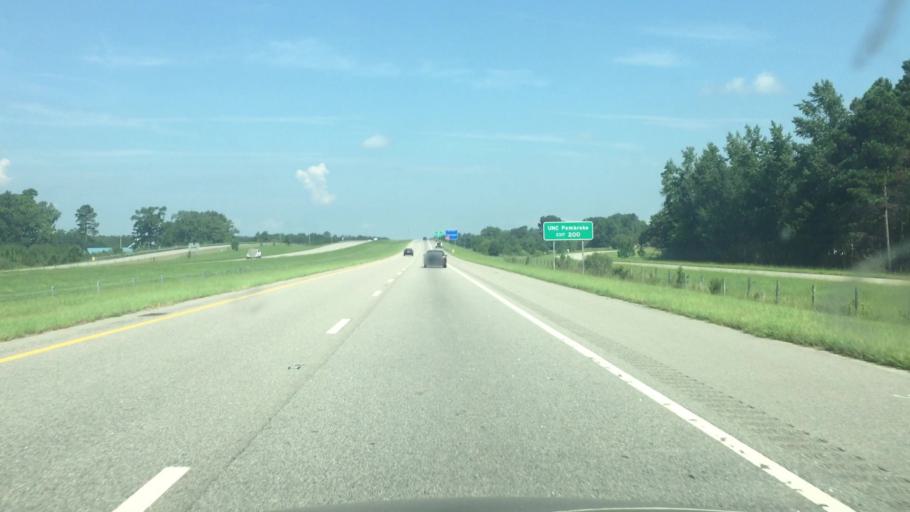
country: US
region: North Carolina
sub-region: Robeson County
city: Pembroke
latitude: 34.6458
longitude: -79.2398
